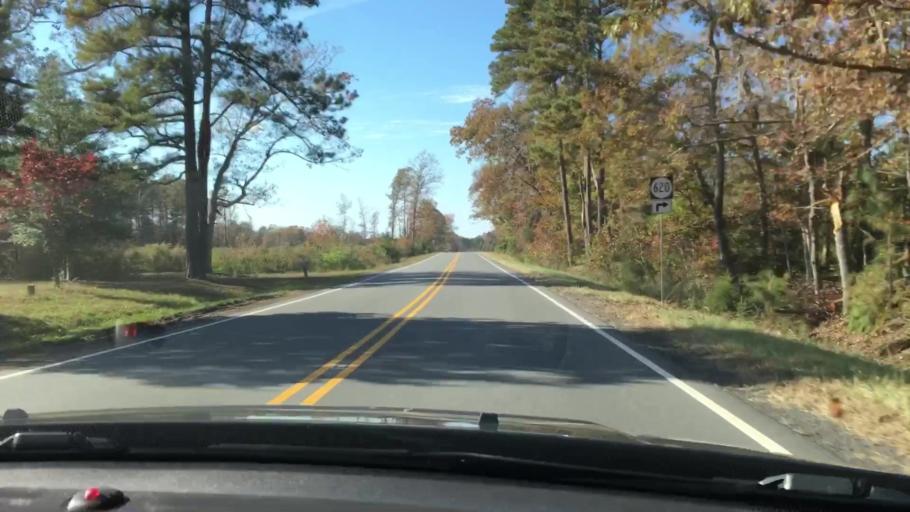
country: US
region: Virginia
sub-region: King William County
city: King William
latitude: 37.6752
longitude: -76.9850
